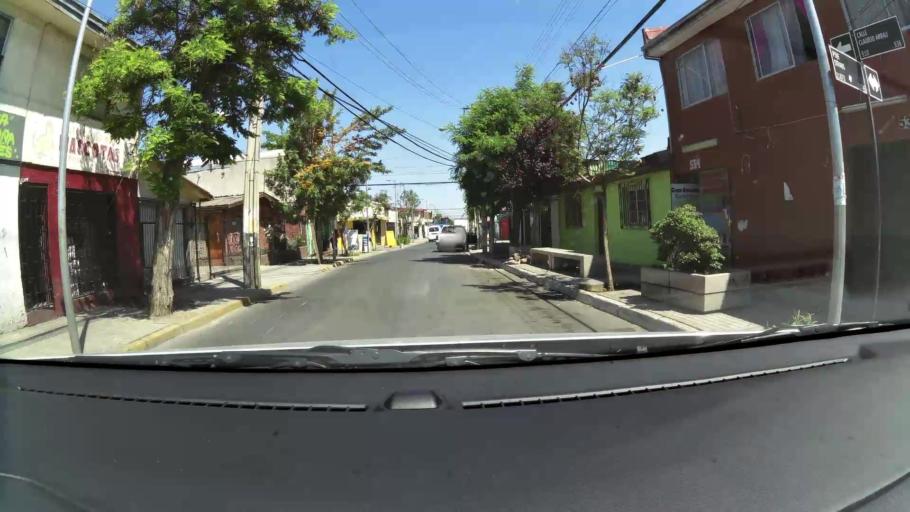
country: CL
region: Santiago Metropolitan
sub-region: Provincia de Maipo
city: San Bernardo
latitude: -33.5655
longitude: -70.6775
